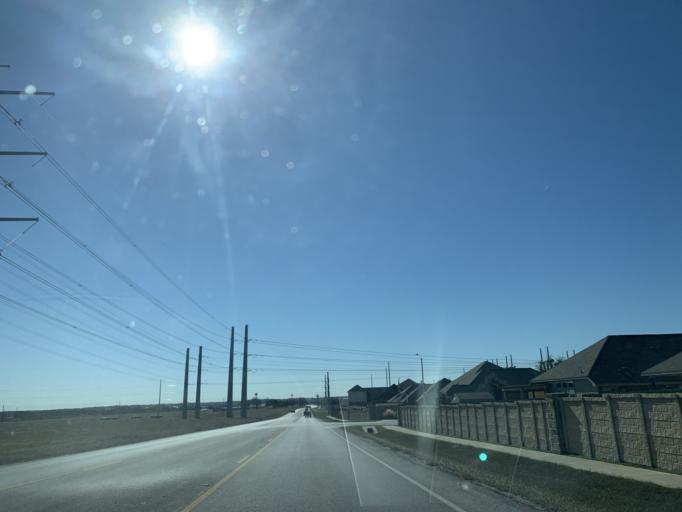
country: US
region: Texas
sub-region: Williamson County
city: Hutto
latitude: 30.5544
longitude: -97.5596
